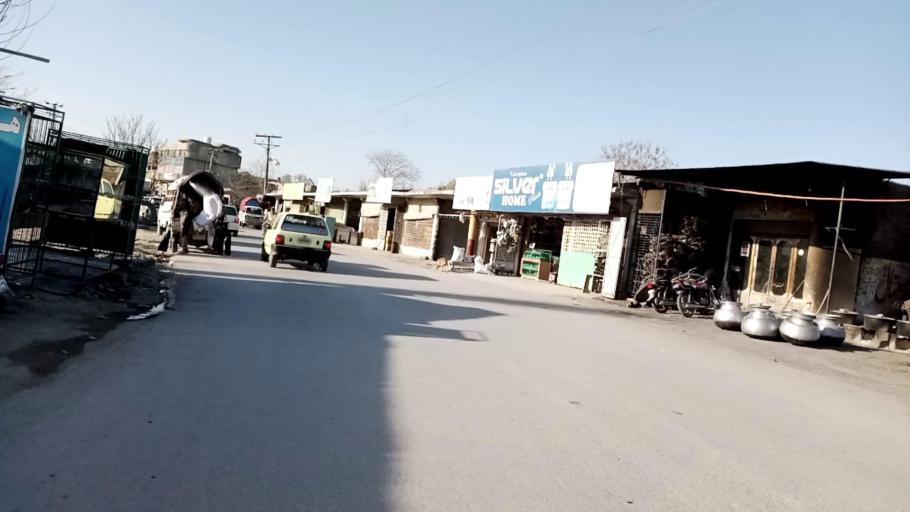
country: PK
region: Khyber Pakhtunkhwa
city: Peshawar
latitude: 34.0881
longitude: 71.5305
